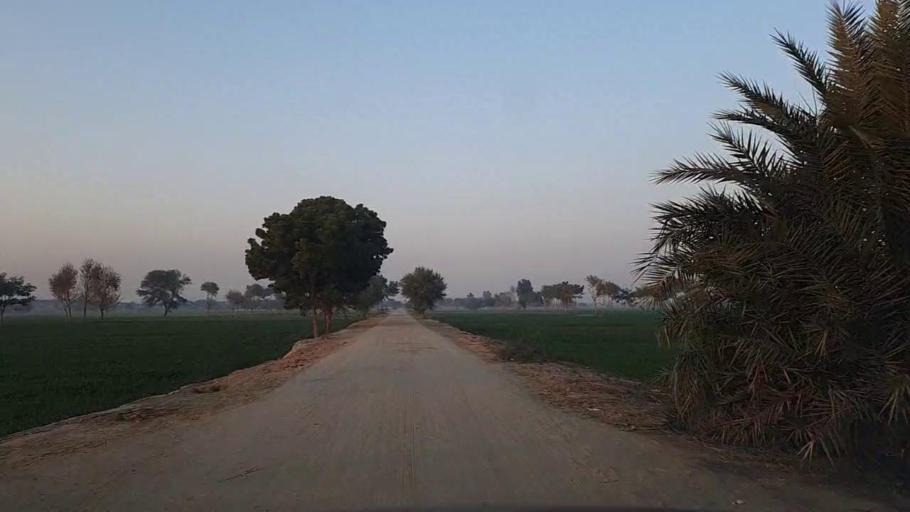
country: PK
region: Sindh
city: Jam Sahib
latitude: 26.4645
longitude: 68.5419
